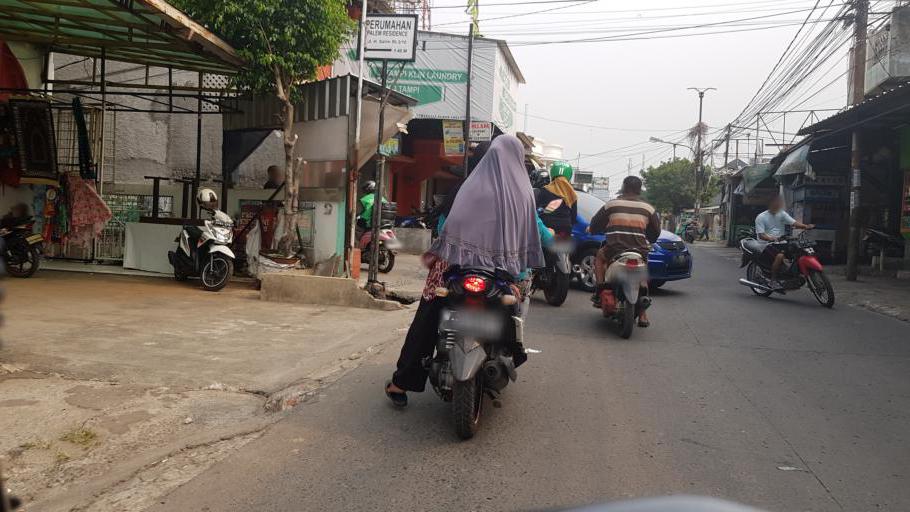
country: ID
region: West Java
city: Depok
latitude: -6.3602
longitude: 106.8431
